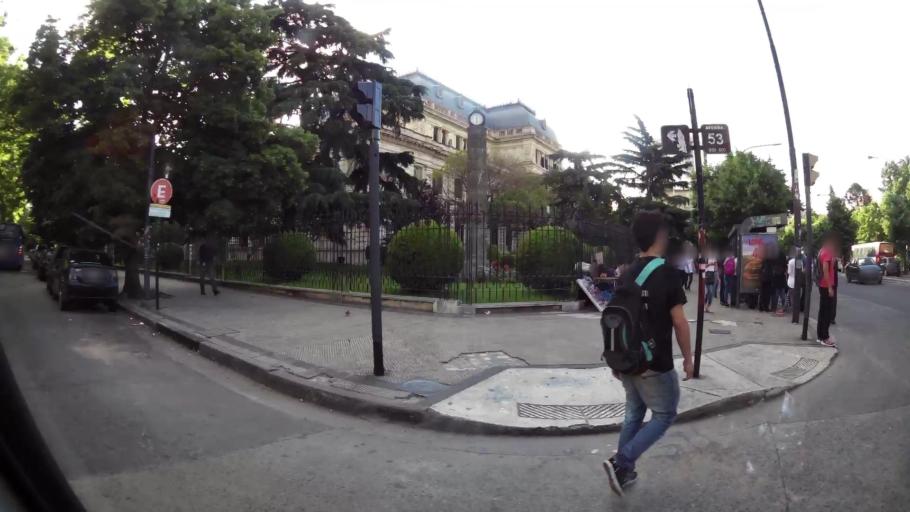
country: AR
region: Buenos Aires
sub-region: Partido de La Plata
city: La Plata
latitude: -34.9163
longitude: -57.9479
